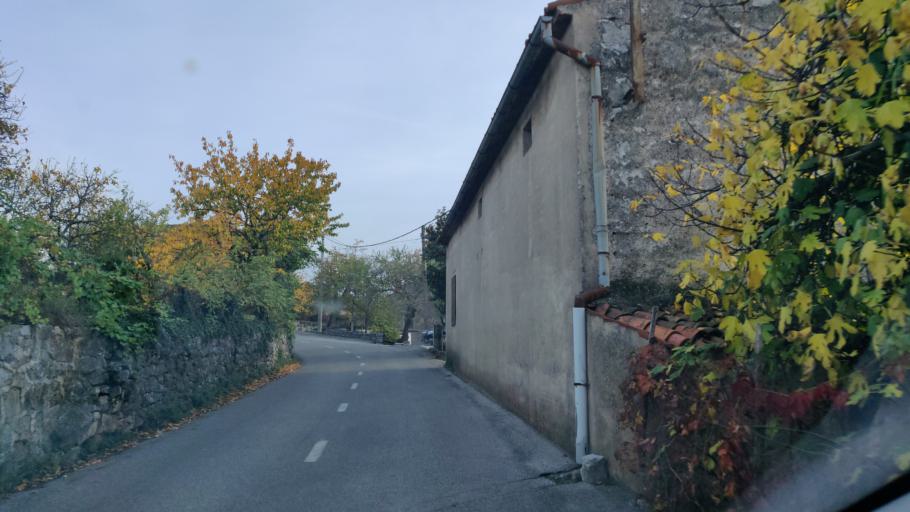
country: SI
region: Miren-Kostanjevica
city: Bilje
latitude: 45.8451
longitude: 13.6397
